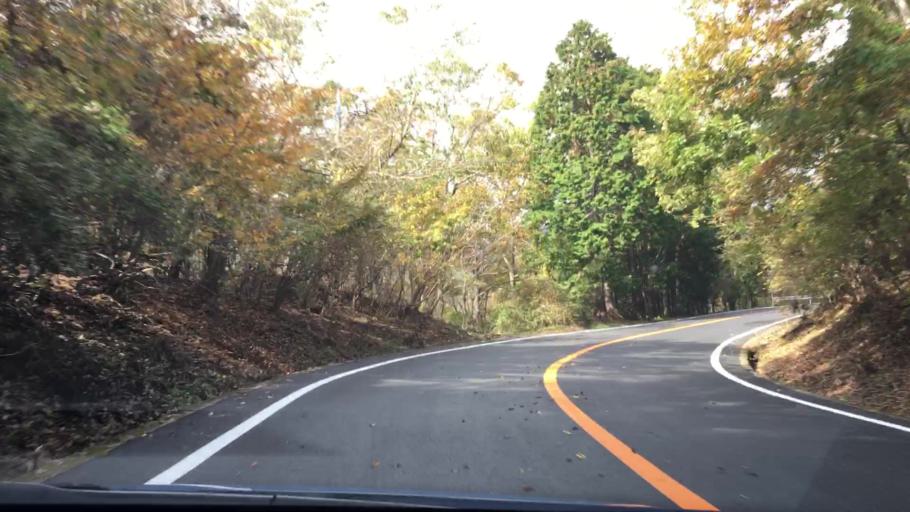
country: JP
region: Shizuoka
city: Gotemba
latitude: 35.3817
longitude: 138.9429
